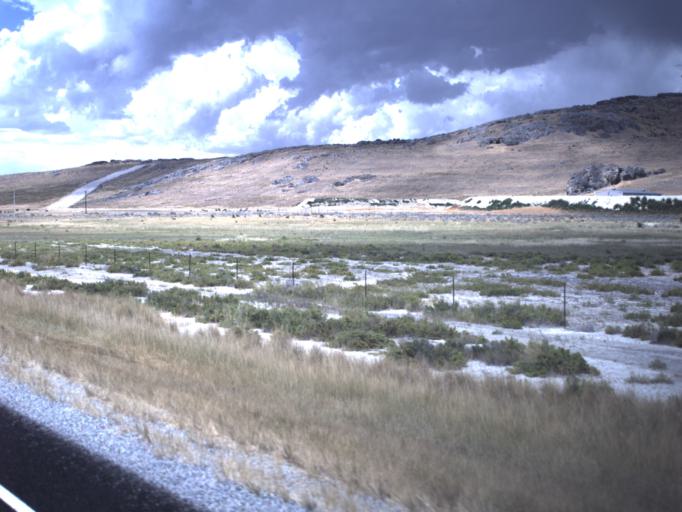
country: US
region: Utah
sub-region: Box Elder County
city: Tremonton
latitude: 41.6277
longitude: -112.4028
